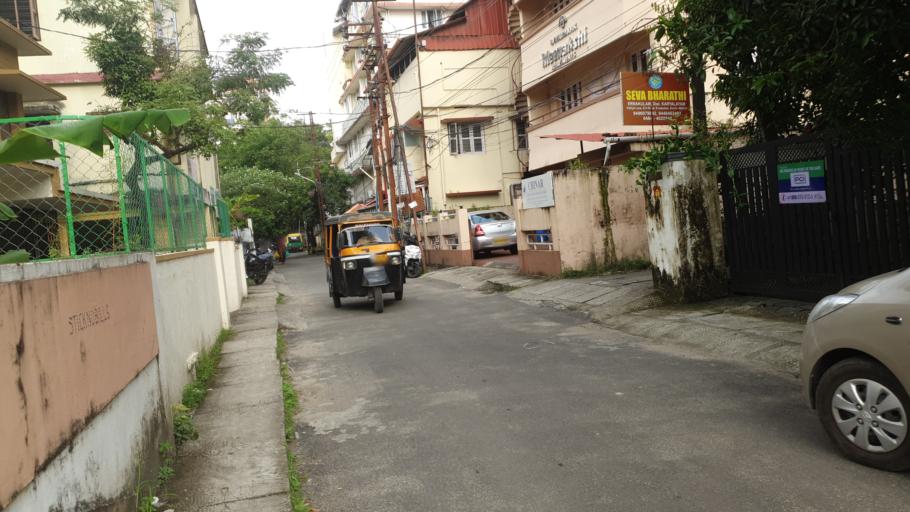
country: IN
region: Kerala
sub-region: Ernakulam
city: Cochin
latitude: 9.9665
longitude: 76.2831
